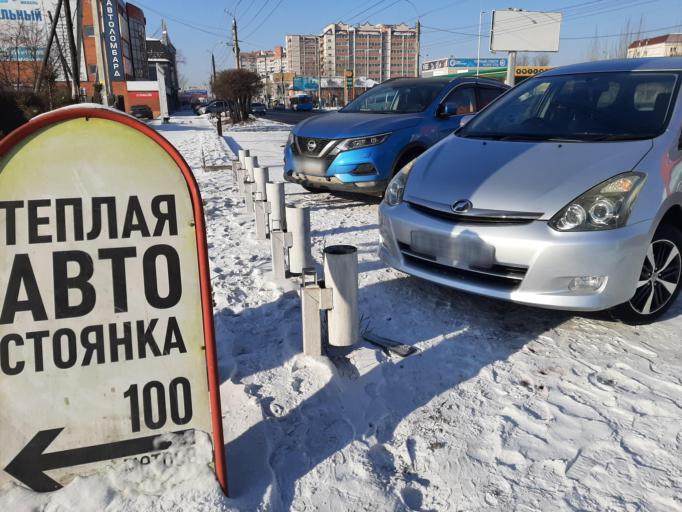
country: RU
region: Transbaikal Territory
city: Chita
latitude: 52.0391
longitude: 113.4858
